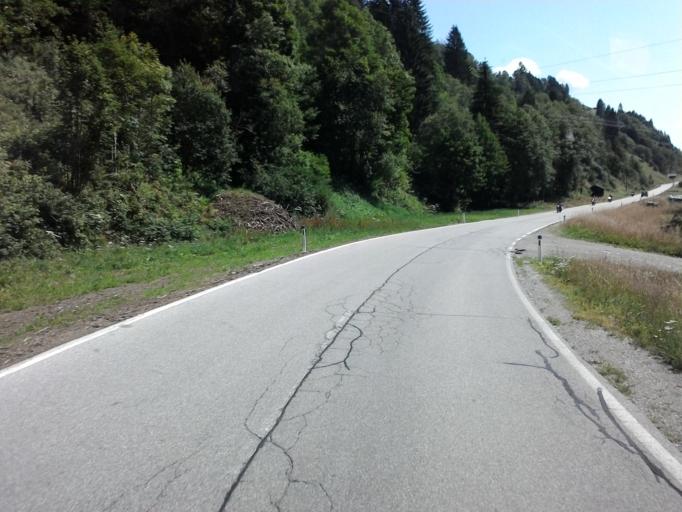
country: AT
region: Tyrol
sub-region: Politischer Bezirk Lienz
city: Untertilliach
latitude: 46.7054
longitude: 12.7053
